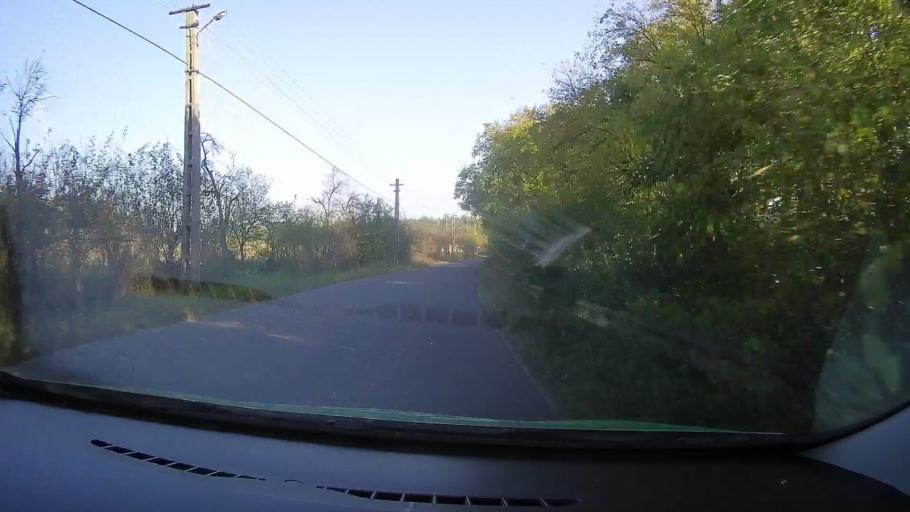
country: RO
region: Arad
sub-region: Comuna Silindia
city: Silindia
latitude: 46.3346
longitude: 21.9314
